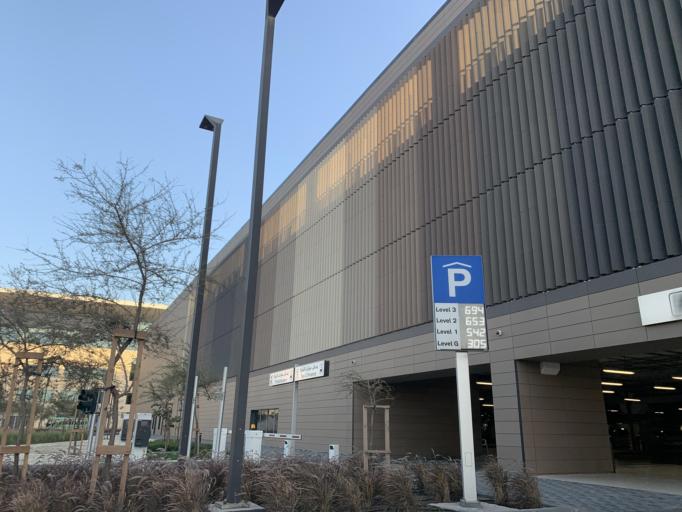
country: BH
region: Muharraq
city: Al Muharraq
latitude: 26.2677
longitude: 50.6281
